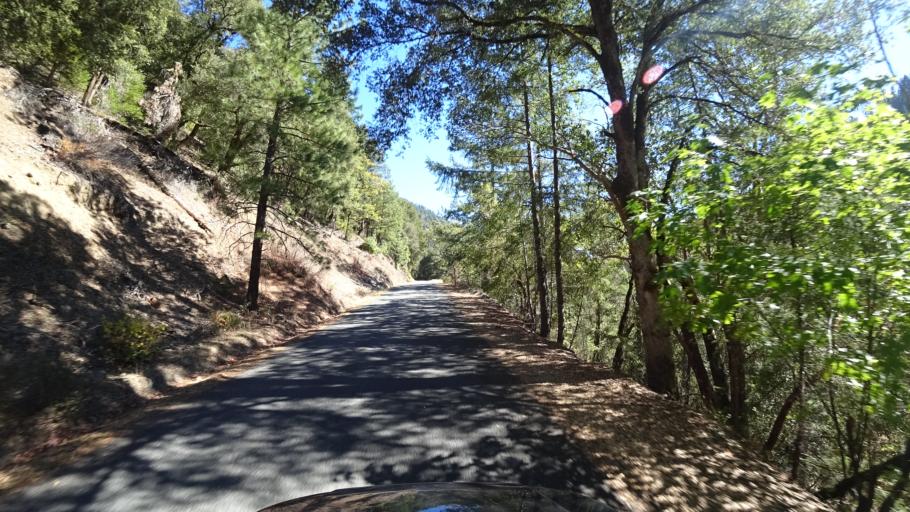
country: US
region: California
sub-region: Humboldt County
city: Willow Creek
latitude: 41.2848
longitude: -123.3594
